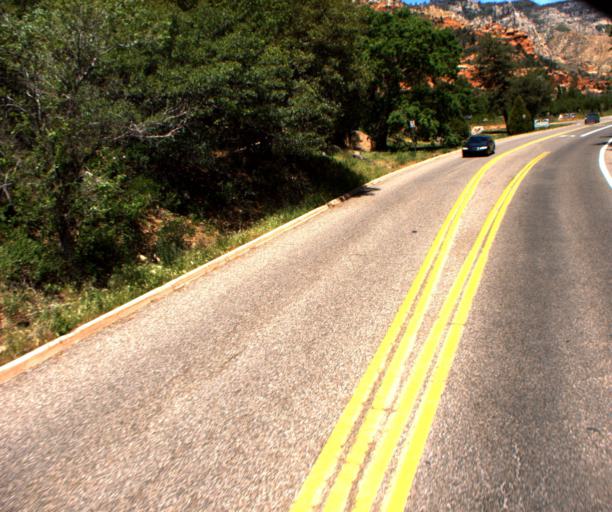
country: US
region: Arizona
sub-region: Coconino County
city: Sedona
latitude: 34.9432
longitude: -111.7524
